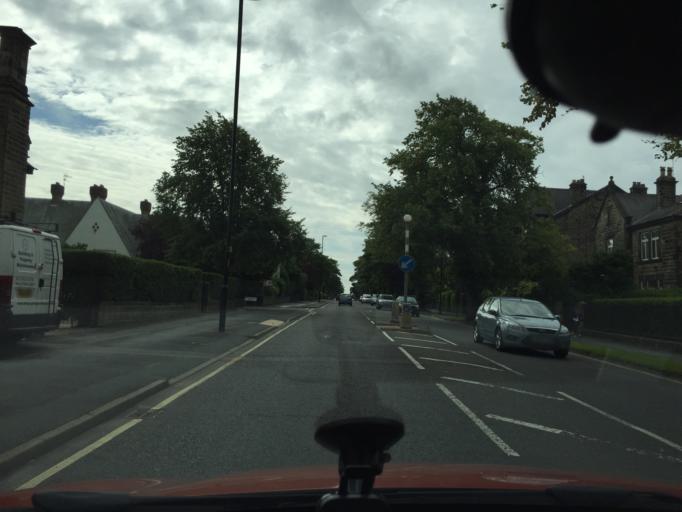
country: GB
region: England
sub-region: North Yorkshire
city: Harrogate
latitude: 53.9811
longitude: -1.5358
